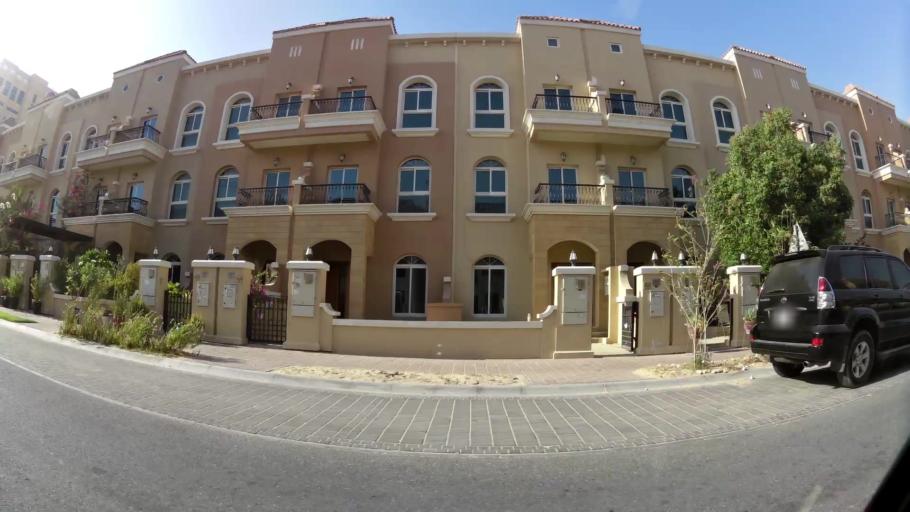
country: AE
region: Dubai
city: Dubai
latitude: 25.0656
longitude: 55.2116
